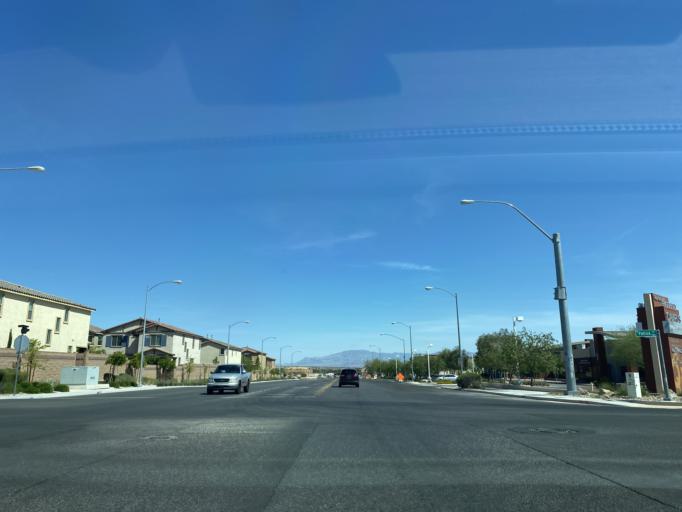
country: US
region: Nevada
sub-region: Clark County
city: Spring Valley
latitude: 36.0774
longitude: -115.2608
